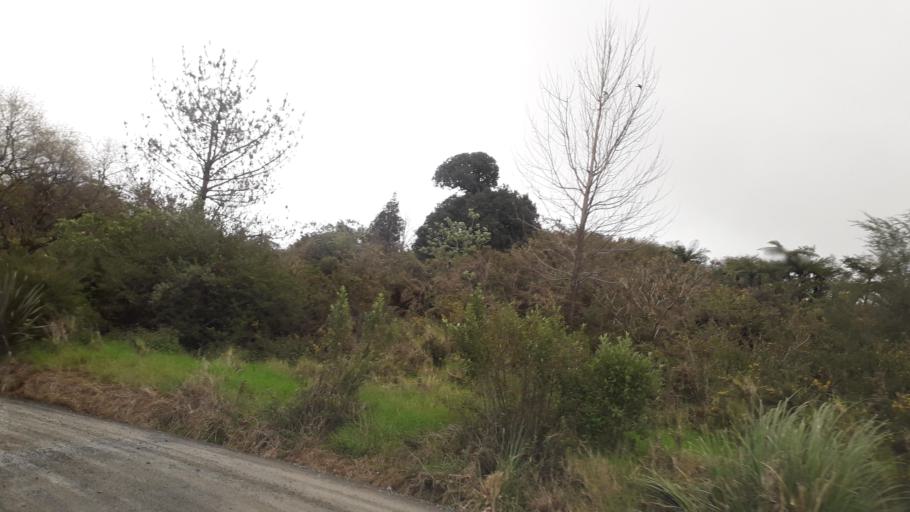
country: NZ
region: Northland
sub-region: Far North District
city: Kerikeri
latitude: -35.1215
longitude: 173.7469
